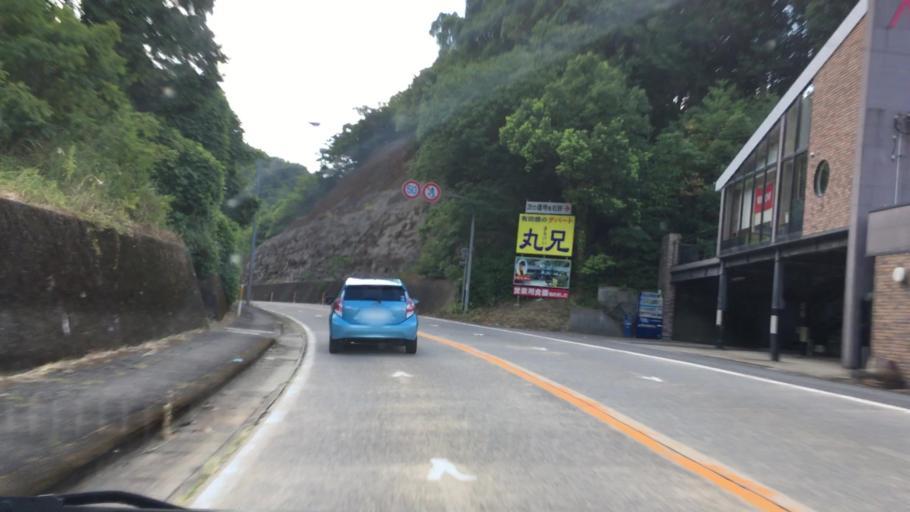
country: JP
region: Saga Prefecture
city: Imaricho-ko
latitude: 33.1910
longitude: 129.9082
